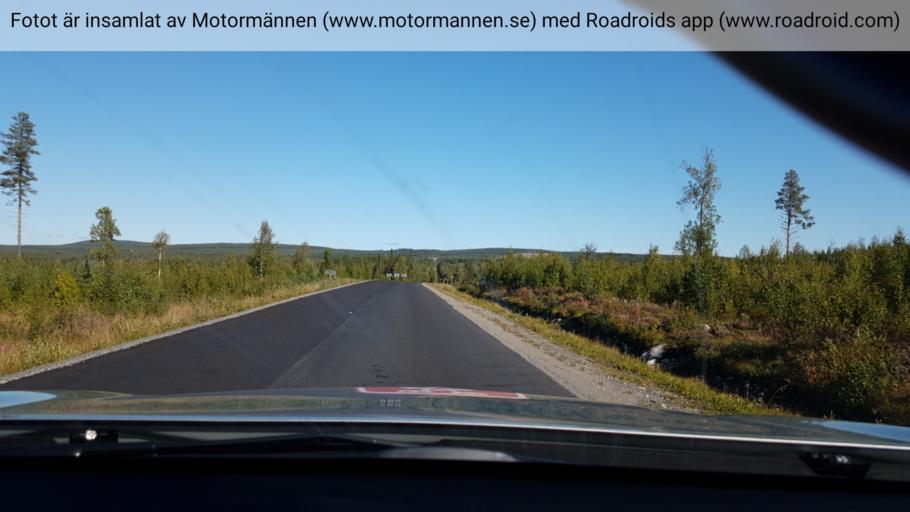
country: SE
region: Vaesterbotten
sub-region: Norsjo Kommun
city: Norsjoe
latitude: 64.8157
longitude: 19.4007
